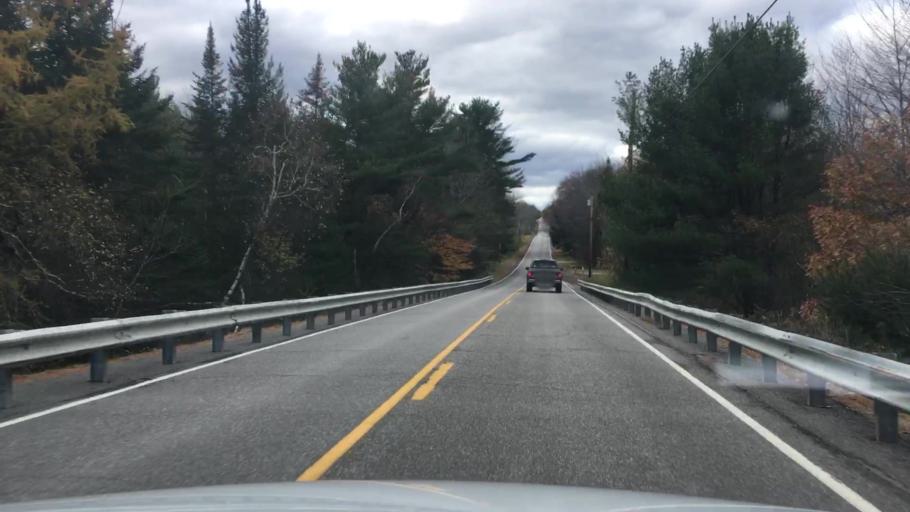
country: US
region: Maine
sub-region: Kennebec County
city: Monmouth
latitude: 44.1315
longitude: -69.9563
